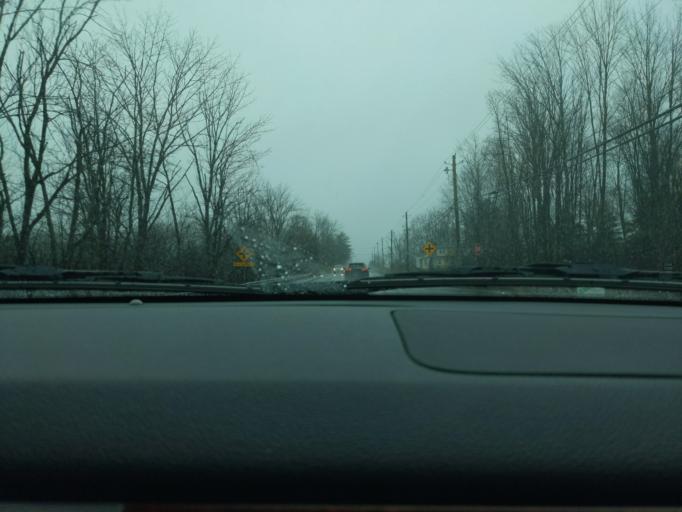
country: US
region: Pennsylvania
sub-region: Bucks County
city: Perkasie
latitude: 40.4146
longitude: -75.2691
